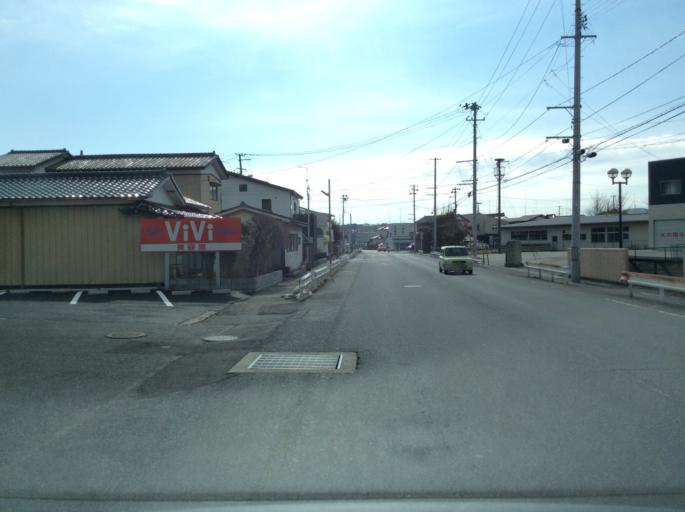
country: JP
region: Fukushima
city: Iwaki
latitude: 36.9538
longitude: 140.9046
